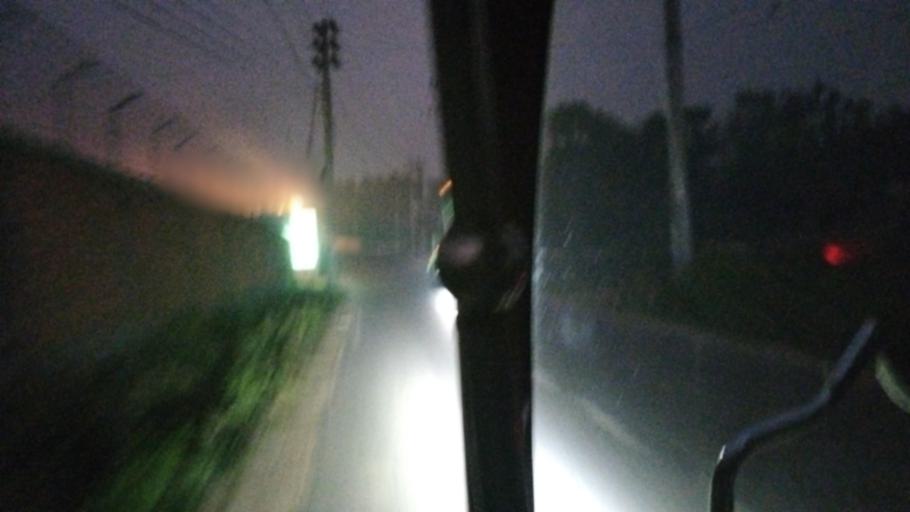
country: BD
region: Dhaka
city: Sakhipur
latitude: 24.4017
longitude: 90.3539
